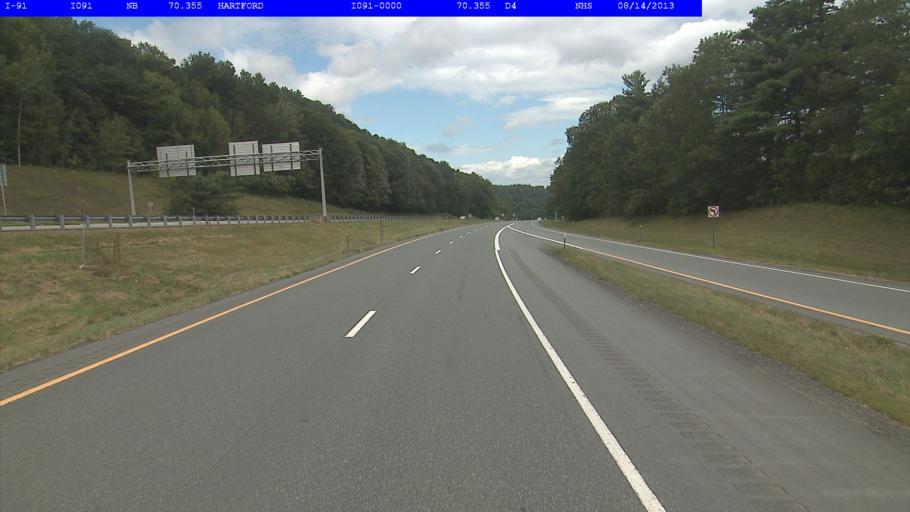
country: US
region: Vermont
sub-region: Windsor County
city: White River Junction
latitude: 43.6476
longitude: -72.3368
